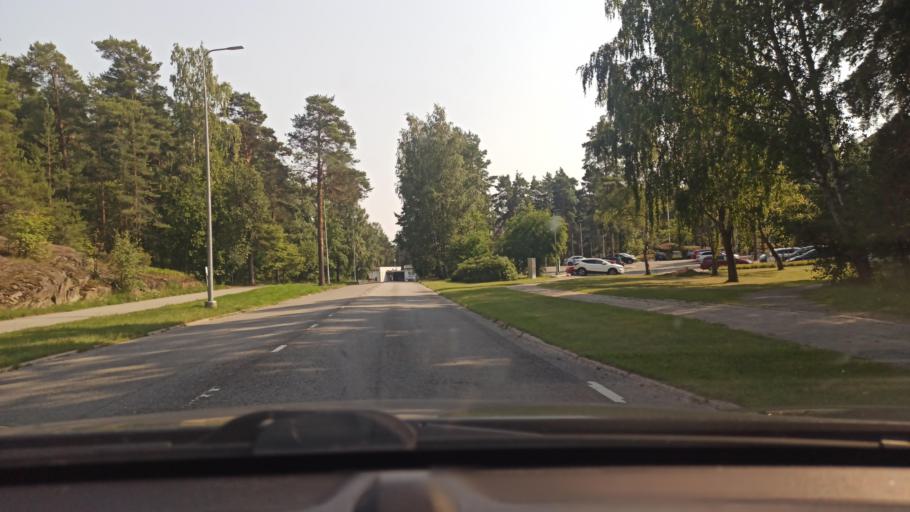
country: FI
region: Varsinais-Suomi
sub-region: Turku
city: Turku
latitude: 60.4626
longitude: 22.2178
